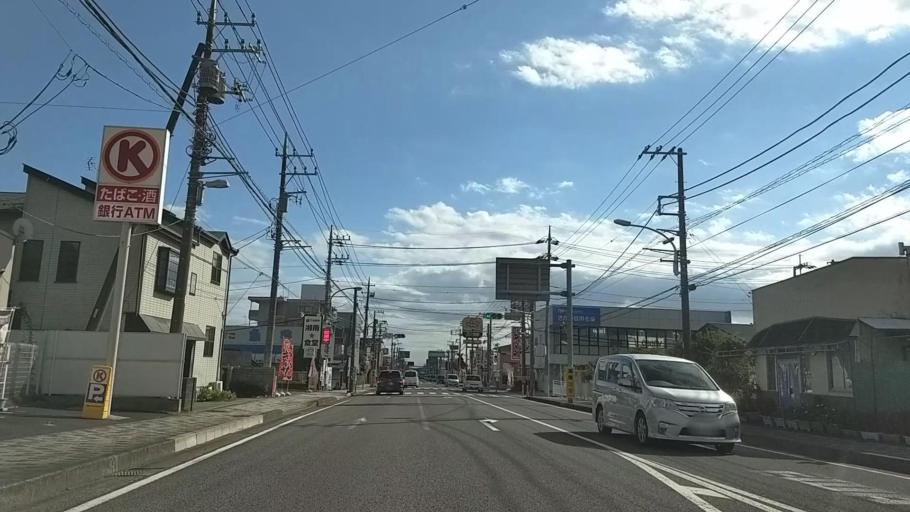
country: JP
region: Kanagawa
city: Hadano
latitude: 35.3376
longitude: 139.1527
